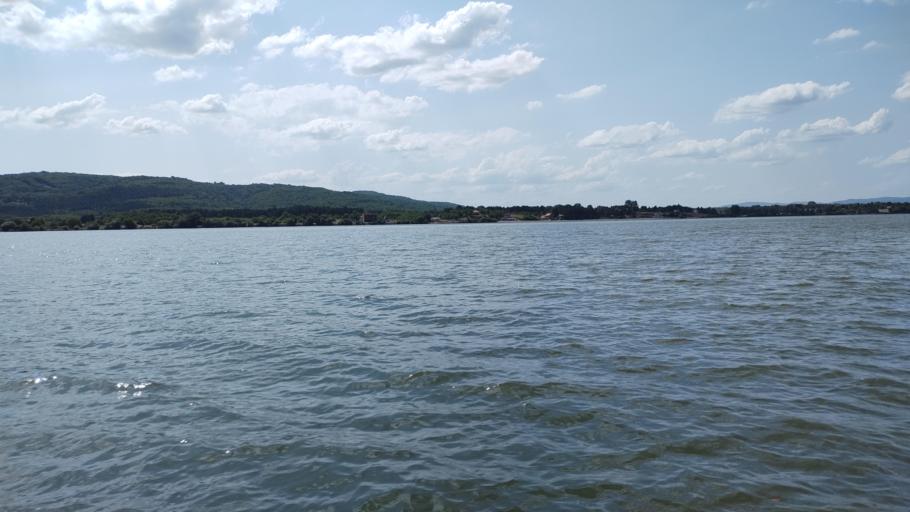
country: RS
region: Central Serbia
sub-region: Branicevski Okrug
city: Golubac
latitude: 44.6738
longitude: 21.6182
